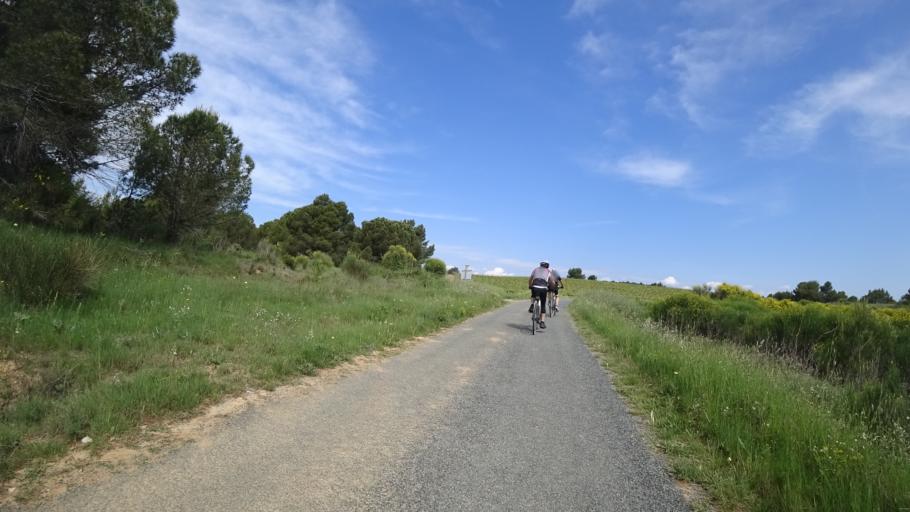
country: FR
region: Languedoc-Roussillon
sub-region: Departement de l'Aude
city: Canet
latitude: 43.2575
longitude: 2.8057
